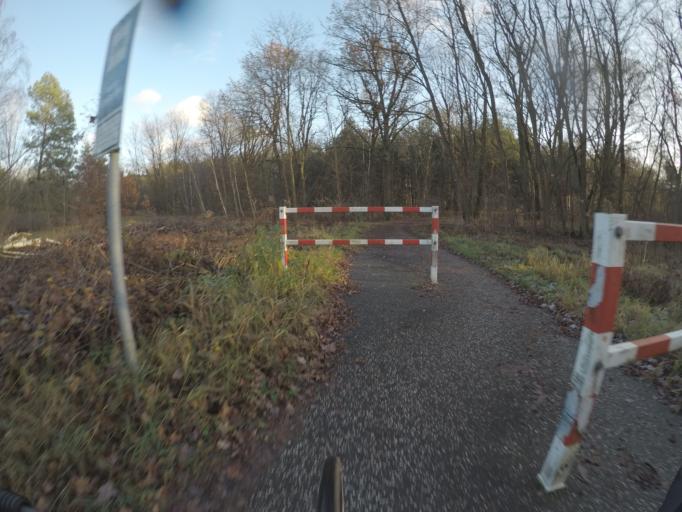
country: DE
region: Brandenburg
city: Hennigsdorf
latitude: 52.6601
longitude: 13.2245
